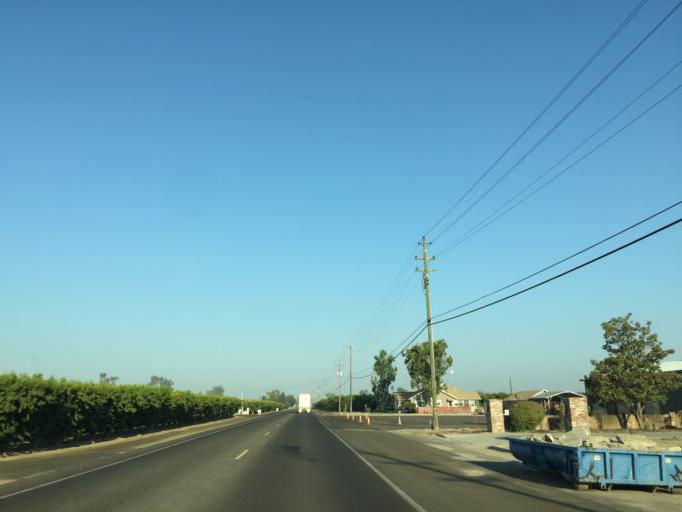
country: US
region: California
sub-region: Fresno County
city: Kingsburg
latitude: 36.4888
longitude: -119.5054
